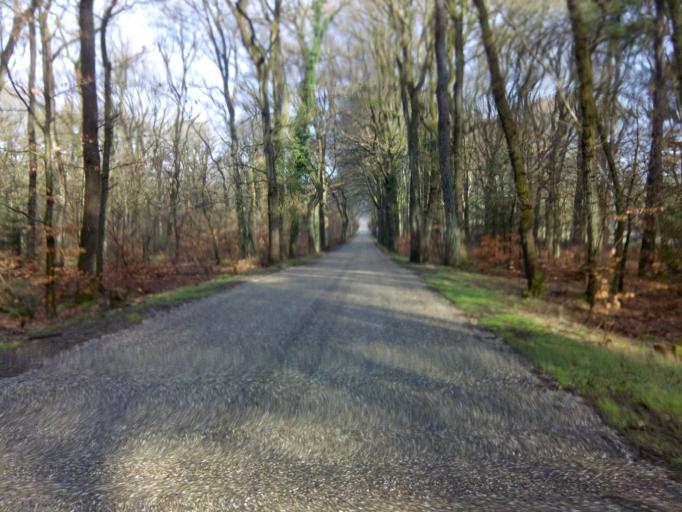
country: NL
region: Utrecht
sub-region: Gemeente Utrechtse Heuvelrug
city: Maarsbergen
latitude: 52.0411
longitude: 5.3977
